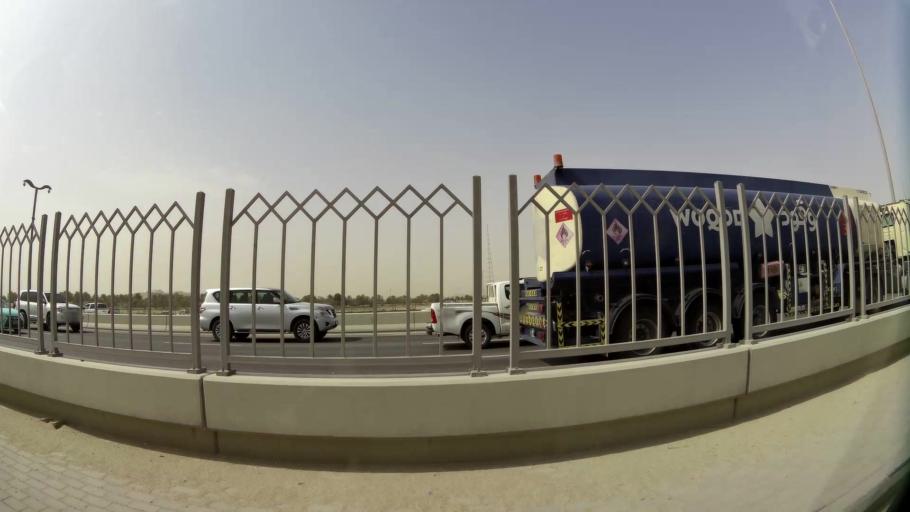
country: QA
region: Baladiyat ad Dawhah
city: Doha
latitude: 25.2886
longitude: 51.4798
